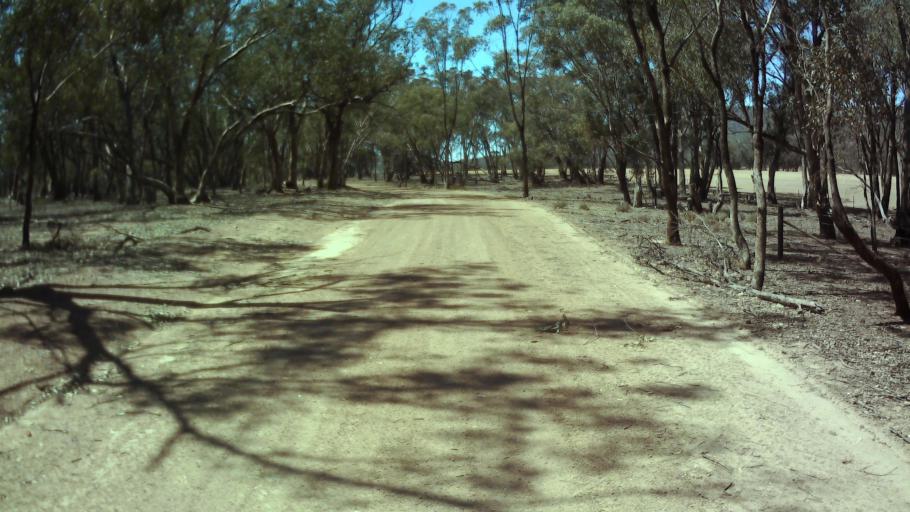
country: AU
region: New South Wales
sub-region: Weddin
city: Grenfell
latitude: -33.9641
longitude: 148.0896
